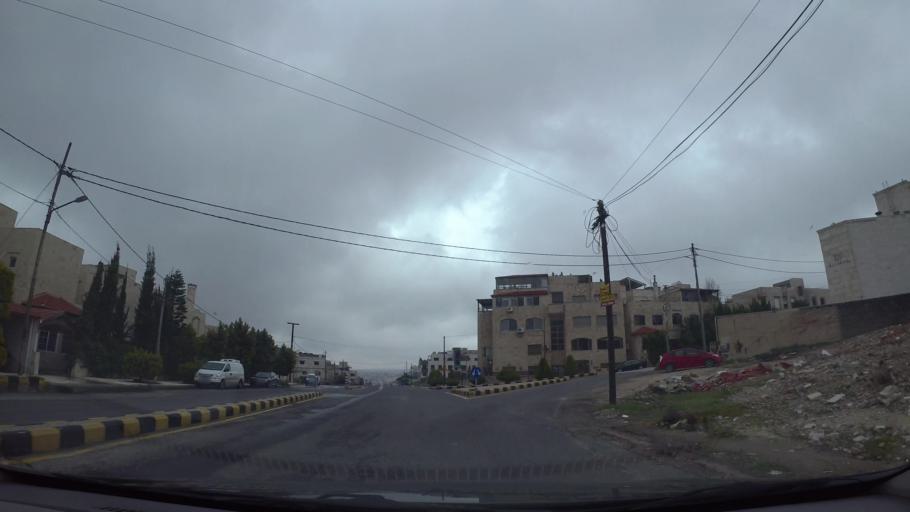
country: JO
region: Amman
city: Al Bunayyat ash Shamaliyah
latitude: 31.9441
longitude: 35.8846
